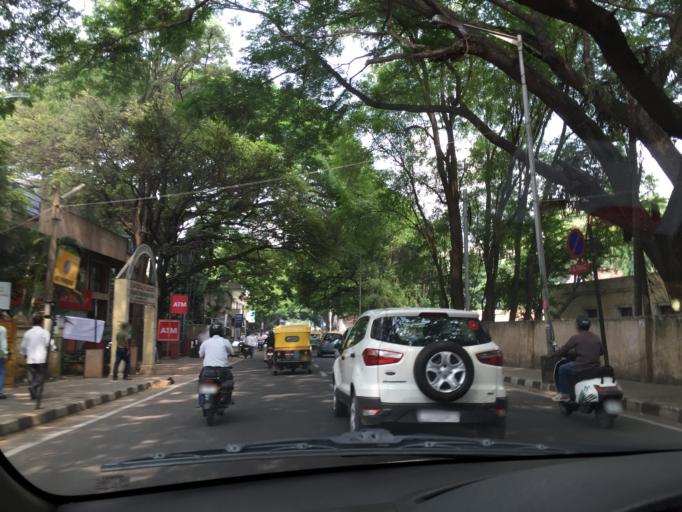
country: IN
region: Karnataka
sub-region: Bangalore Urban
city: Bangalore
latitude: 12.9821
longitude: 77.5989
